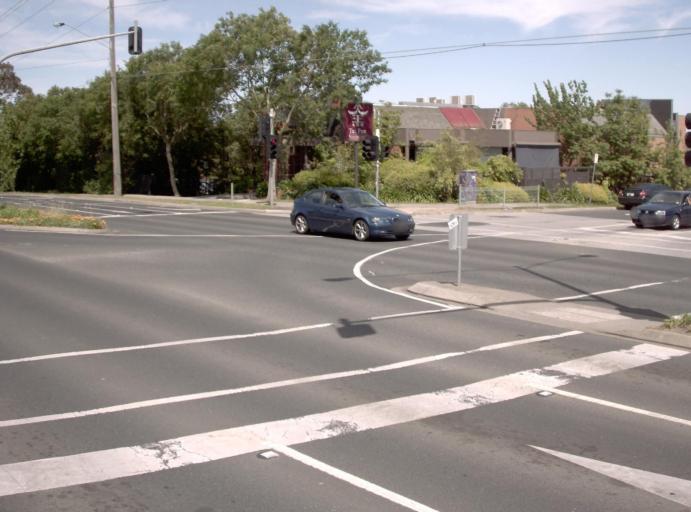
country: AU
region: Victoria
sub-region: Manningham
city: Donvale
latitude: -37.7824
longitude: 145.1633
